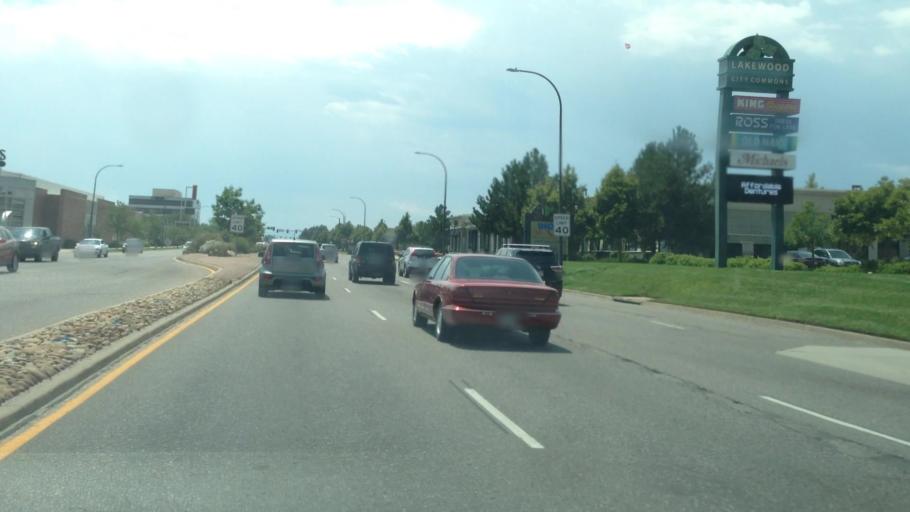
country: US
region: Colorado
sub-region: Jefferson County
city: Lakewood
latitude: 39.7102
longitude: -105.0816
